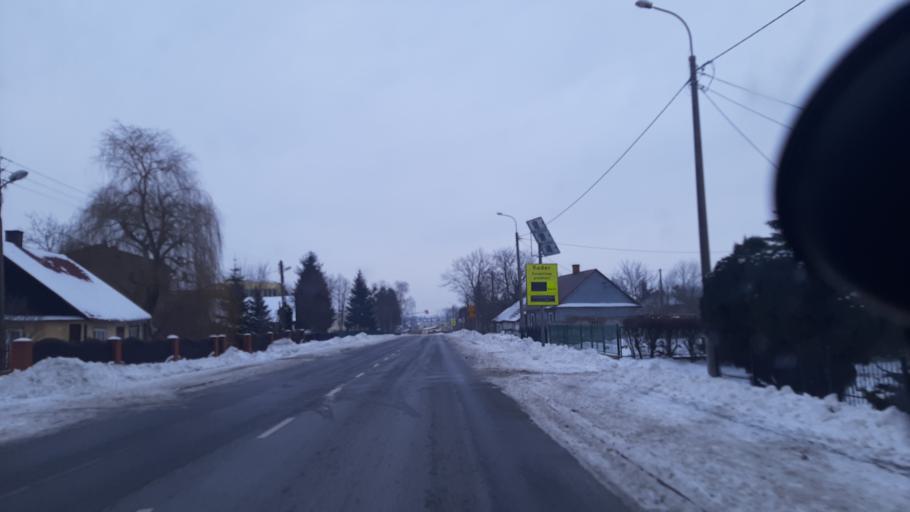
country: PL
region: Lublin Voivodeship
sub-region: Powiat pulawski
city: Markuszow
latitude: 51.3756
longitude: 22.2534
